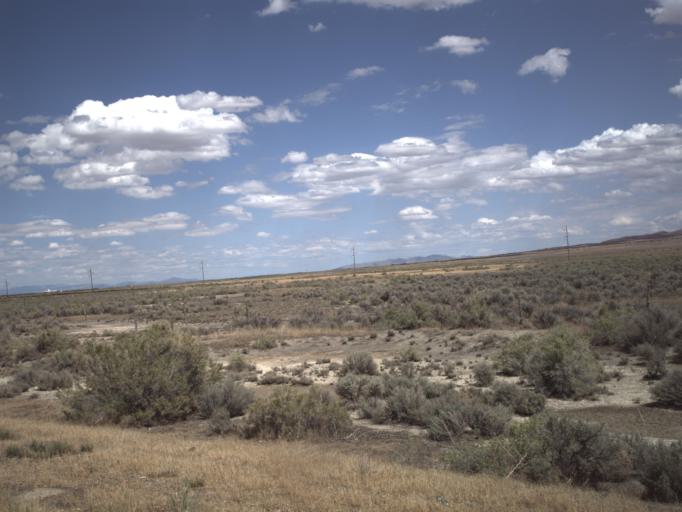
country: US
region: Utah
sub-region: Millard County
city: Delta
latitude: 39.2510
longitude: -112.4397
